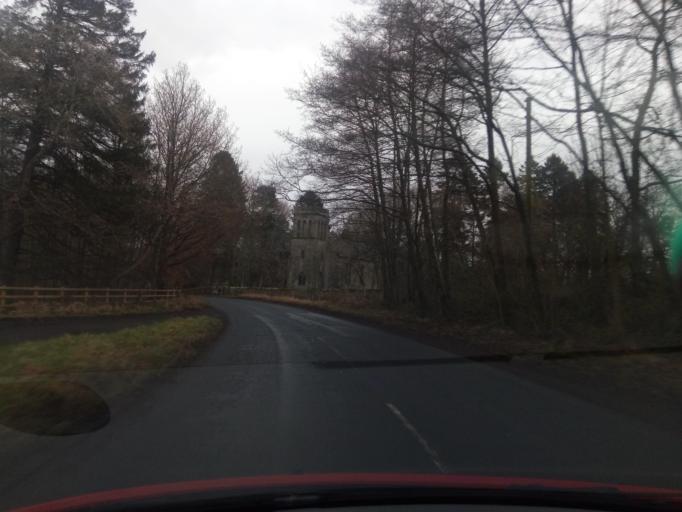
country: GB
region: England
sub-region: Northumberland
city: Rochester
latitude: 55.1658
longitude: -2.3628
